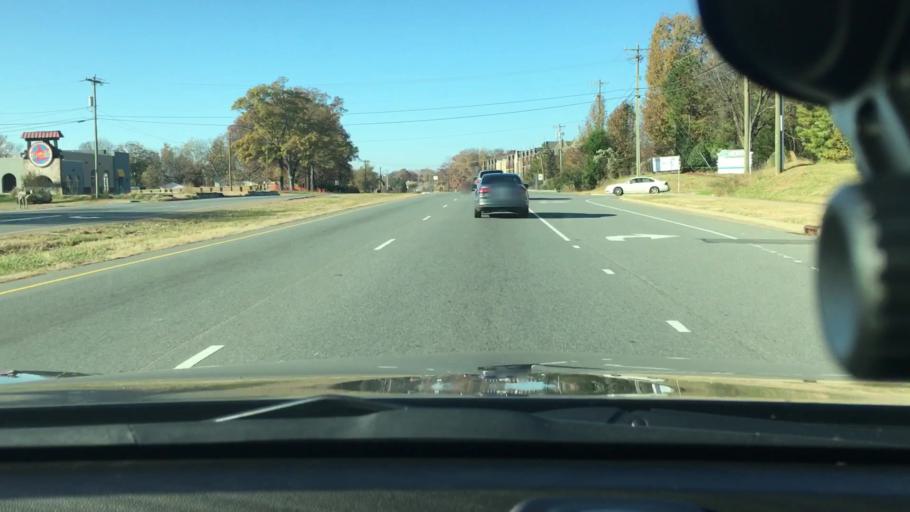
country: US
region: North Carolina
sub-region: Cabarrus County
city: Harrisburg
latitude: 35.3102
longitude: -80.7159
